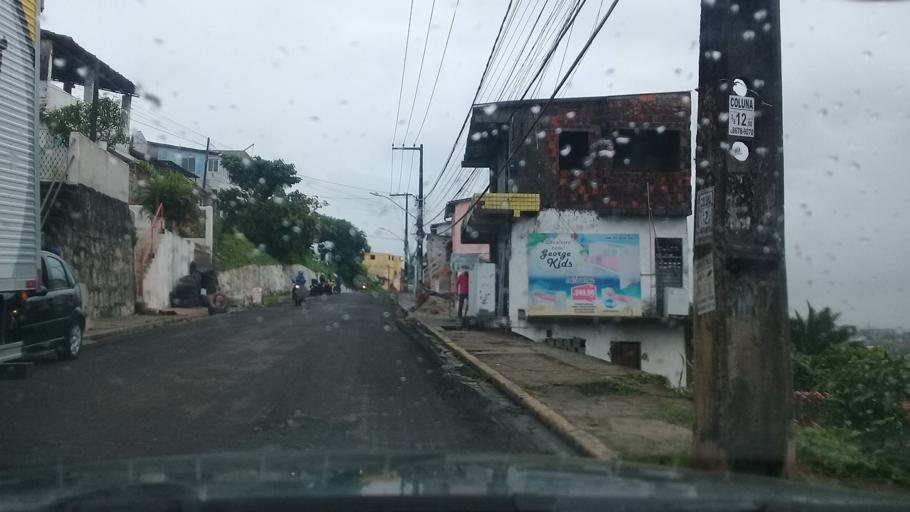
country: BR
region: Pernambuco
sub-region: Jaboatao Dos Guararapes
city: Jaboatao dos Guararapes
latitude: -8.0870
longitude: -34.9753
